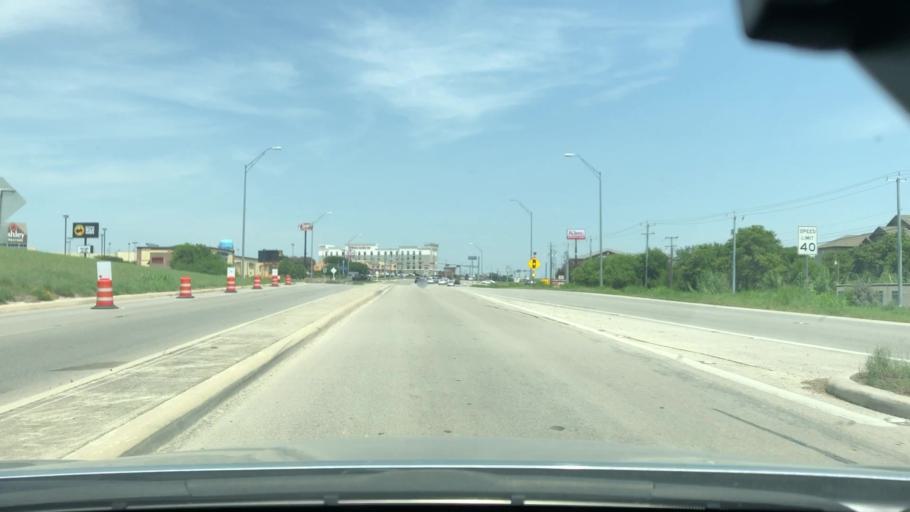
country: US
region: Texas
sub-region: Bexar County
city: Live Oak
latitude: 29.5634
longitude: -98.3367
